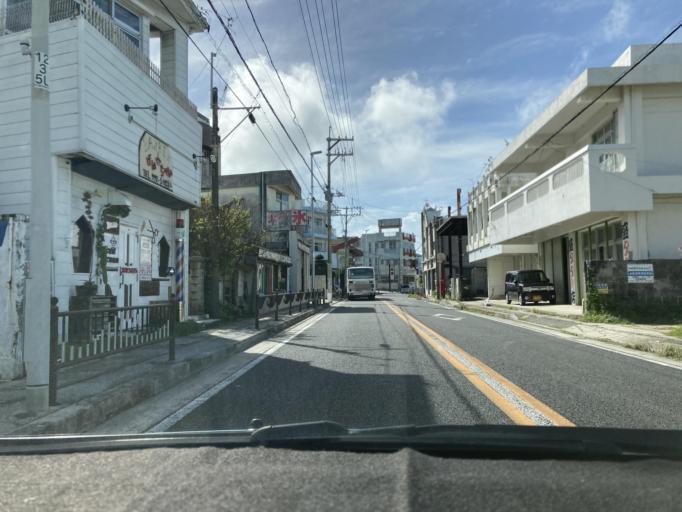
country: JP
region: Okinawa
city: Itoman
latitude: 26.1242
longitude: 127.6698
